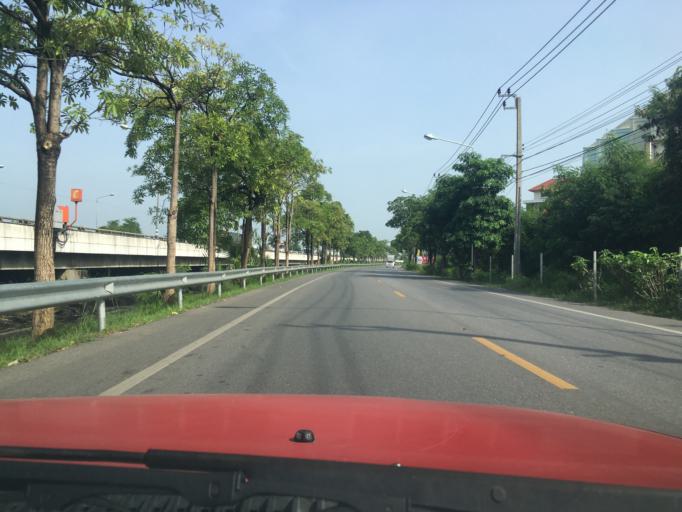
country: TH
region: Bangkok
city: Bang Khun Thian
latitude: 13.6293
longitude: 100.4196
